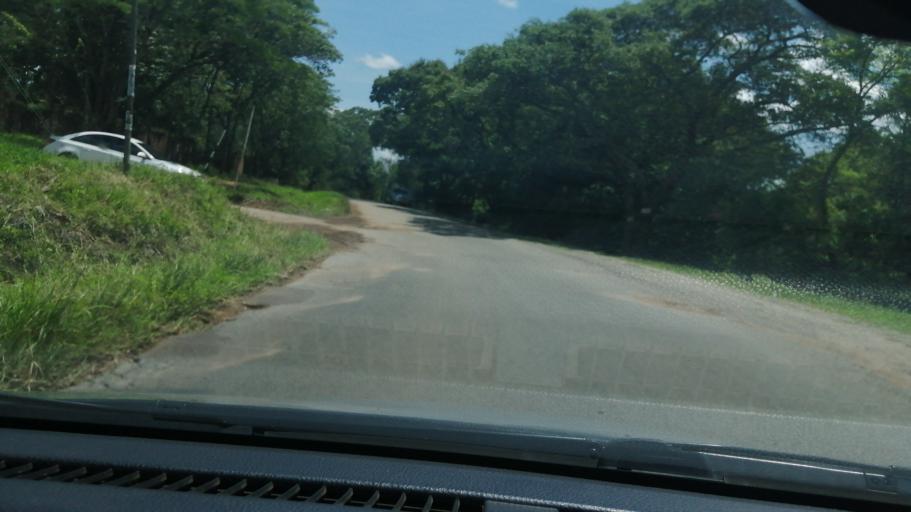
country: ZW
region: Harare
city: Harare
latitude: -17.7724
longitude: 31.0968
